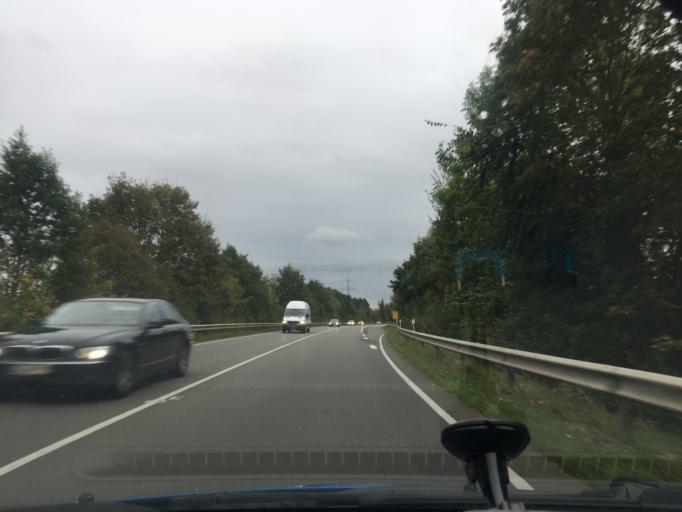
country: DE
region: Lower Saxony
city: Handorf
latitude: 53.3834
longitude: 10.3459
